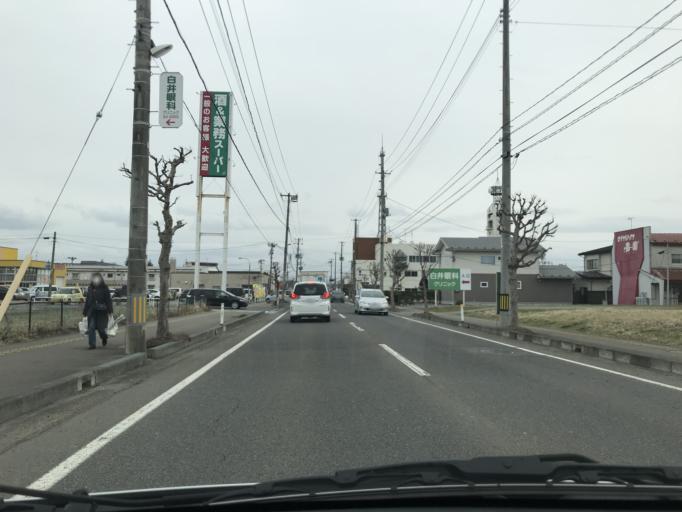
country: JP
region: Iwate
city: Hanamaki
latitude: 39.3878
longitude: 141.1091
